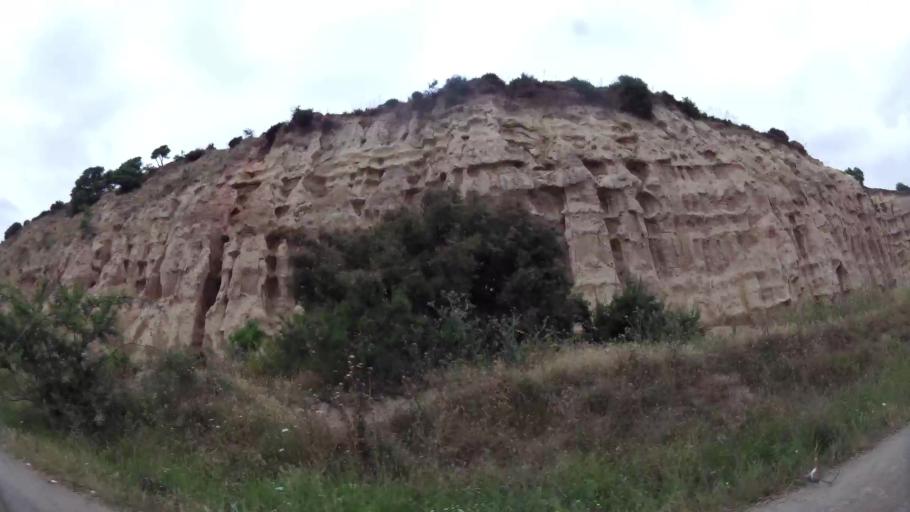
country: MA
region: Rabat-Sale-Zemmour-Zaer
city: Sale
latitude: 34.0054
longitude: -6.7804
